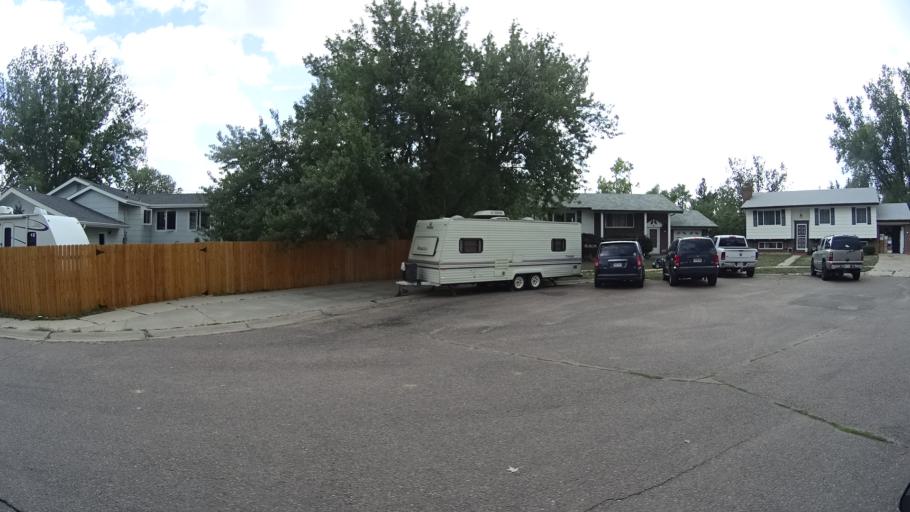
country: US
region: Colorado
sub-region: El Paso County
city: Cimarron Hills
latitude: 38.8494
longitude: -104.7467
